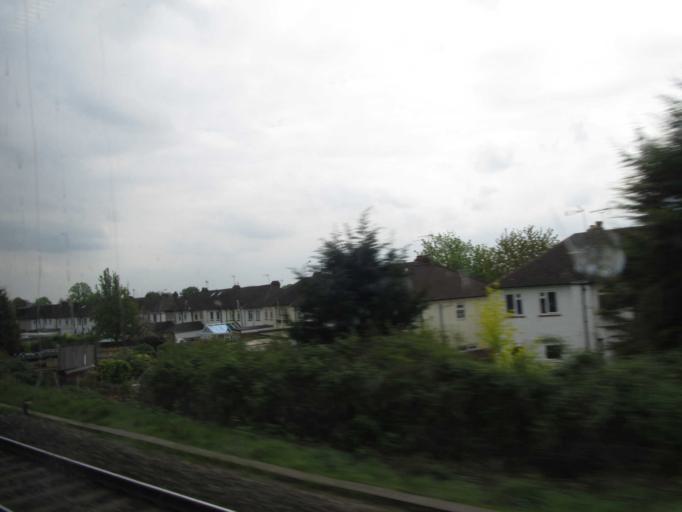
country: GB
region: England
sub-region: Buckinghamshire
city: Farnham Royal
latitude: 51.5234
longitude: -0.6486
